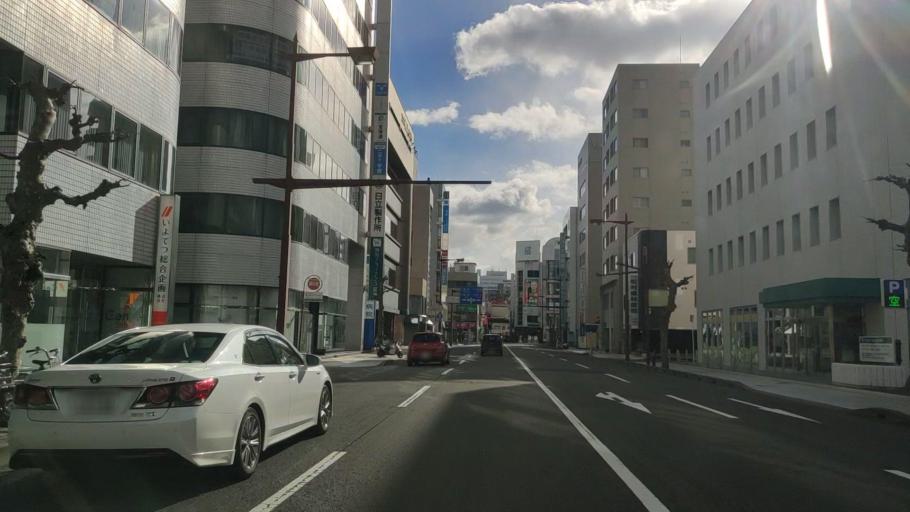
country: JP
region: Ehime
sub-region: Shikoku-chuo Shi
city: Matsuyama
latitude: 33.8380
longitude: 132.7647
